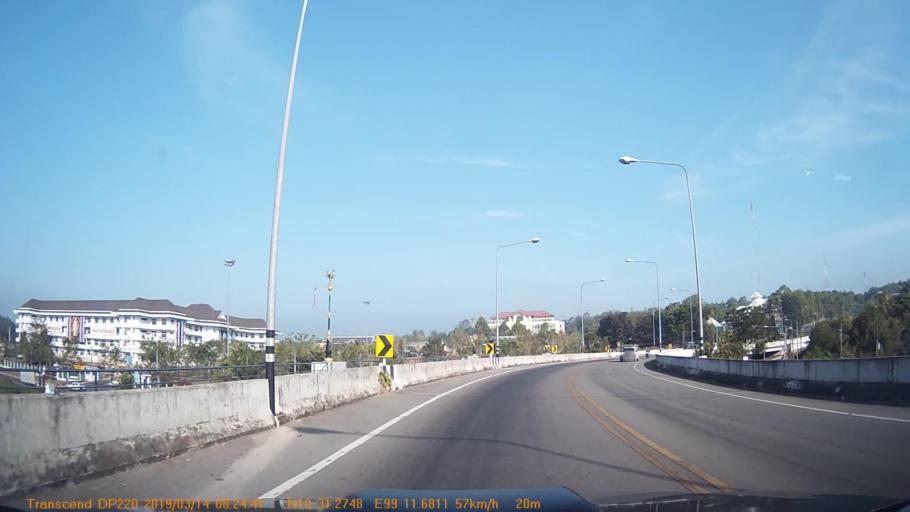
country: TH
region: Chumphon
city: Chumphon
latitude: 10.5213
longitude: 99.1946
